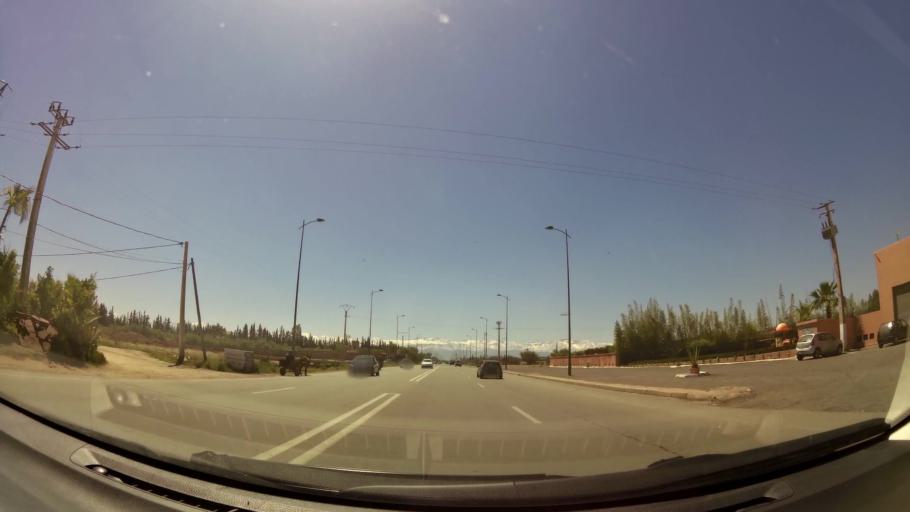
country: MA
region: Marrakech-Tensift-Al Haouz
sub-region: Marrakech
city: Marrakesh
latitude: 31.5574
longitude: -7.9767
